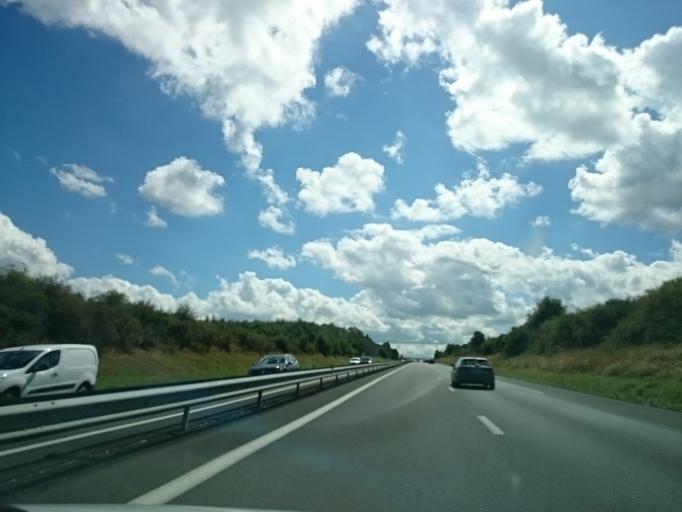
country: FR
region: Pays de la Loire
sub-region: Departement de Maine-et-Loire
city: Durtal
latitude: 47.6434
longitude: -0.2743
